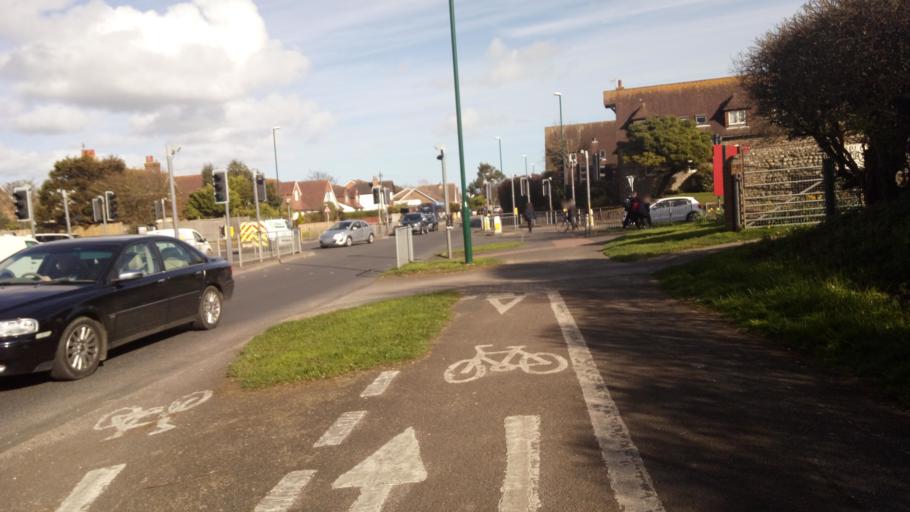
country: GB
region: England
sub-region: West Sussex
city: Bognor Regis
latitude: 50.7923
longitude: -0.6525
